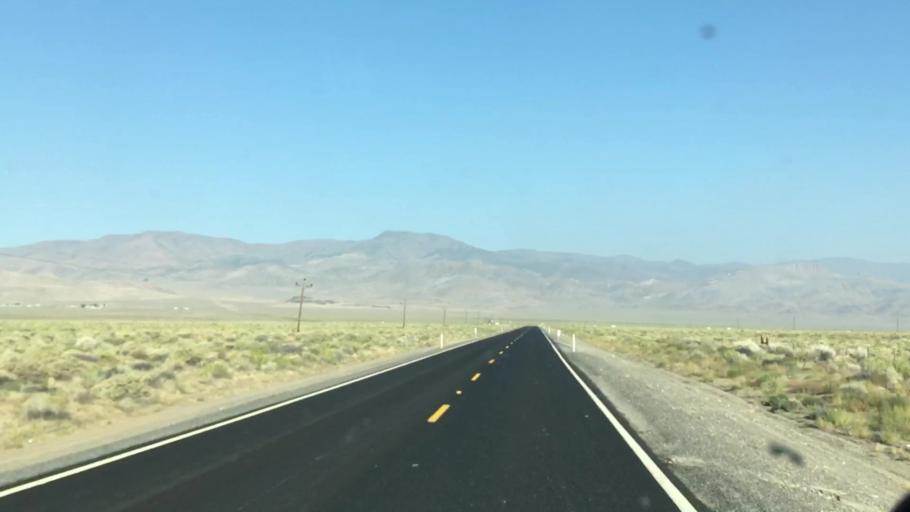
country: US
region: Nevada
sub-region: Lyon County
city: Fernley
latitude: 39.6471
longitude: -119.3152
